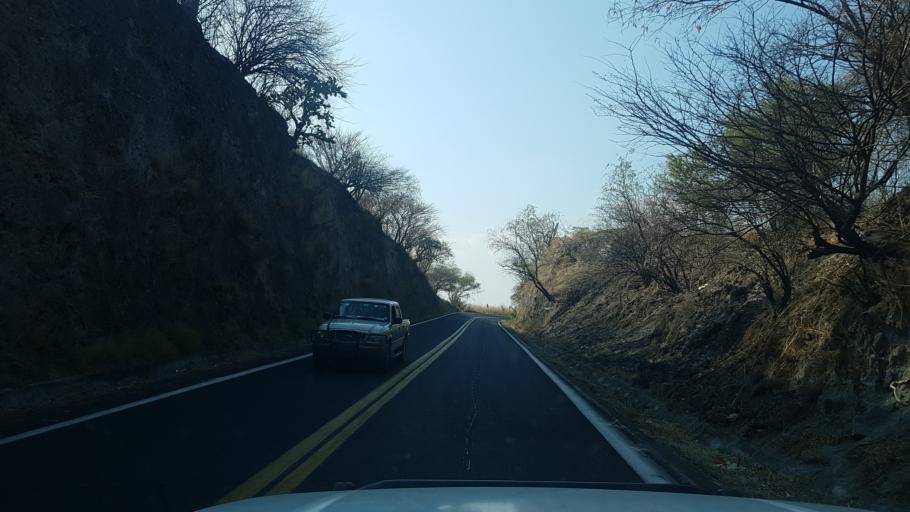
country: MX
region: Puebla
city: Calmeca
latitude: 18.6522
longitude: -98.6641
